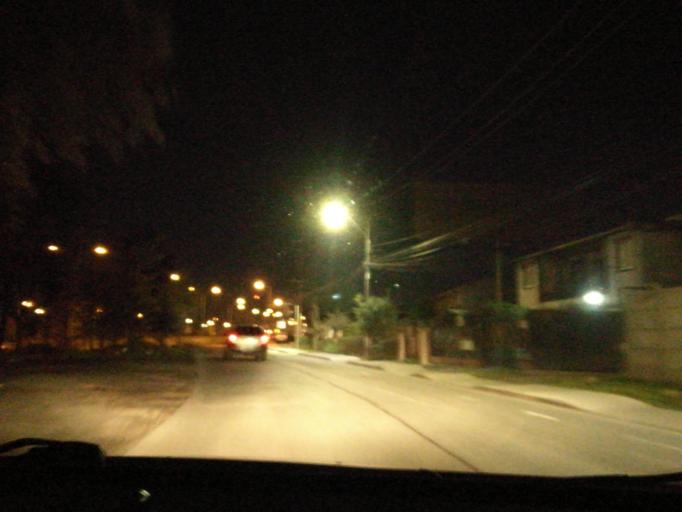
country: CL
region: O'Higgins
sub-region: Provincia de Cachapoal
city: Rancagua
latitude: -34.1841
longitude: -70.7394
